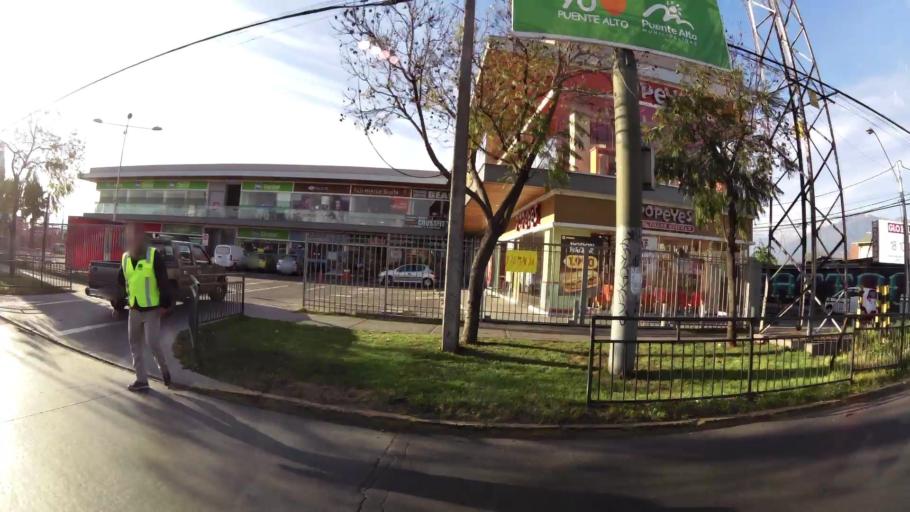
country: CL
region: Santiago Metropolitan
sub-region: Provincia de Cordillera
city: Puente Alto
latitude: -33.6058
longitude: -70.5759
